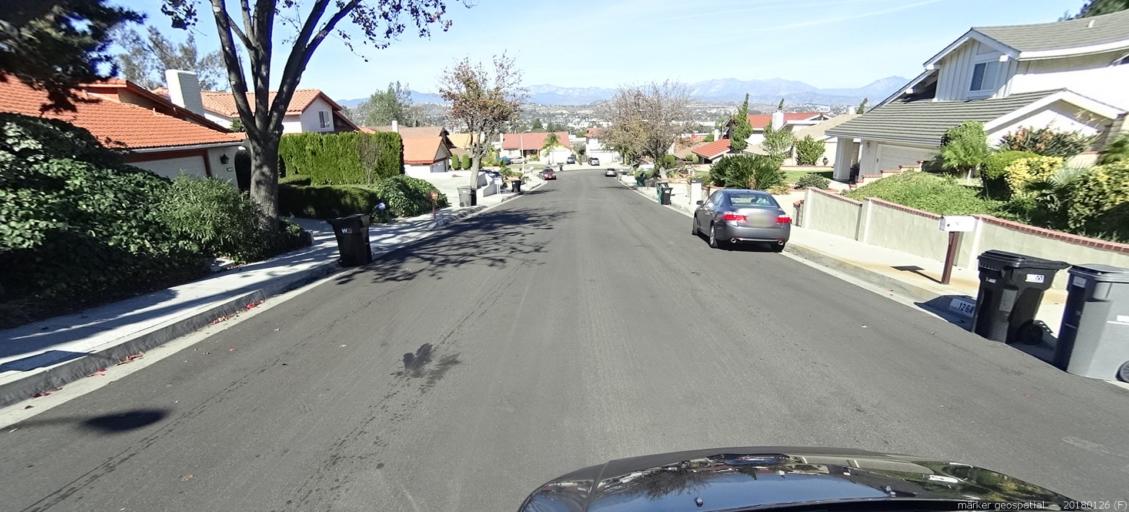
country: US
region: California
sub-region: Los Angeles County
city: Walnut
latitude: 33.9965
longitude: -117.8450
